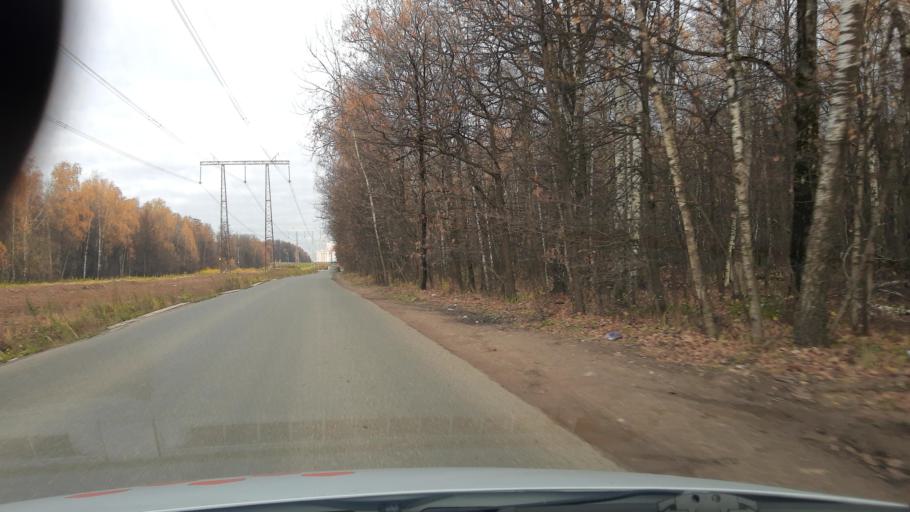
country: RU
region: Moscow
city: Annino
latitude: 55.5418
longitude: 37.6113
